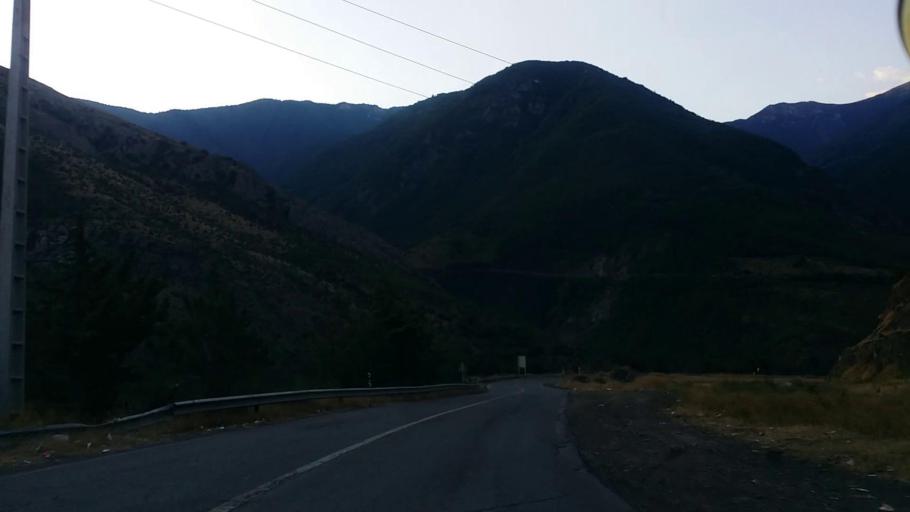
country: IR
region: Mazandaran
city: Chalus
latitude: 36.3897
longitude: 51.2751
